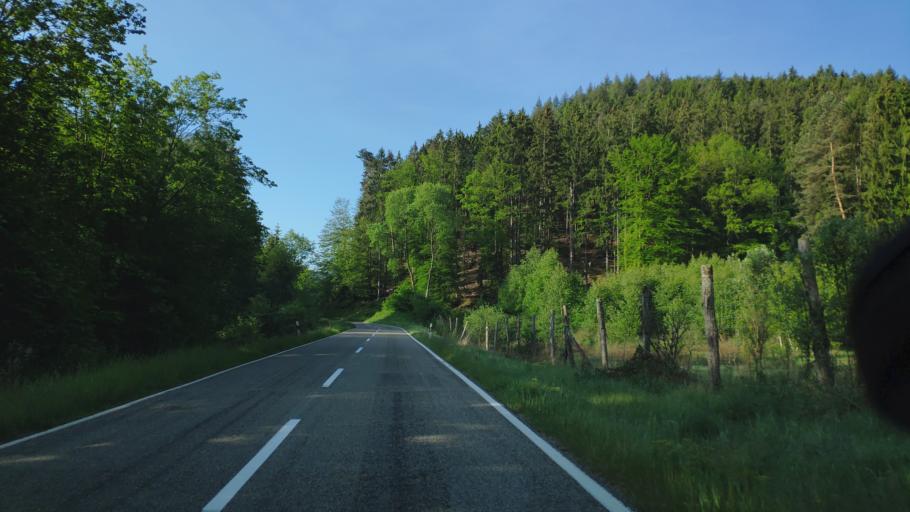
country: DE
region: Rheinland-Pfalz
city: Ruppertsweiler
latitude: 49.1793
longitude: 7.7180
